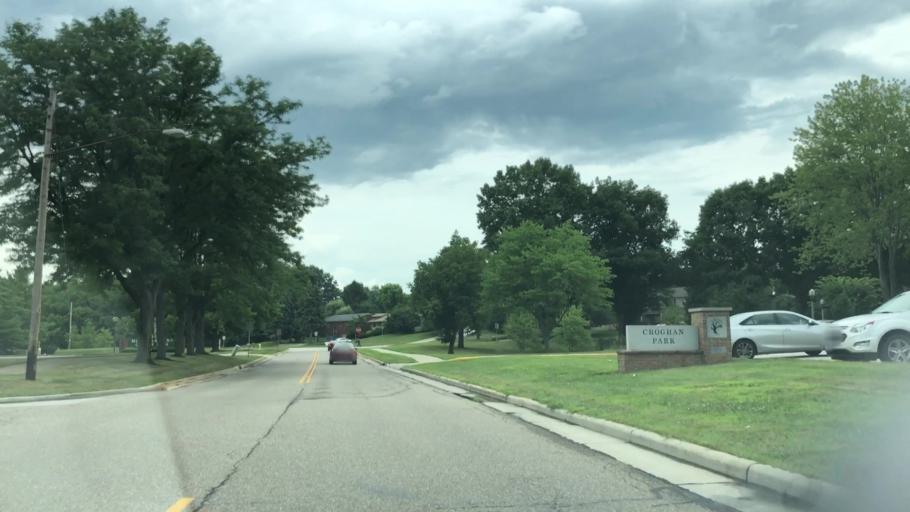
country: US
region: Ohio
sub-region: Summit County
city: Fairlawn
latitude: 41.1313
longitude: -81.6097
